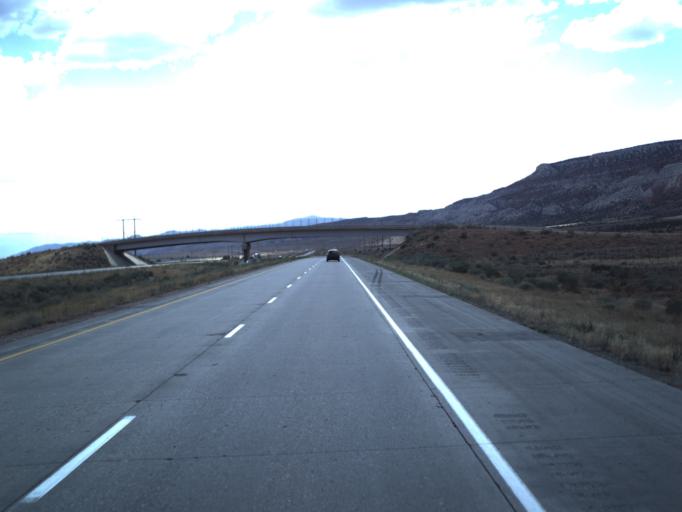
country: US
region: Utah
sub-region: Sevier County
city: Aurora
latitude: 38.8496
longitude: -112.0050
